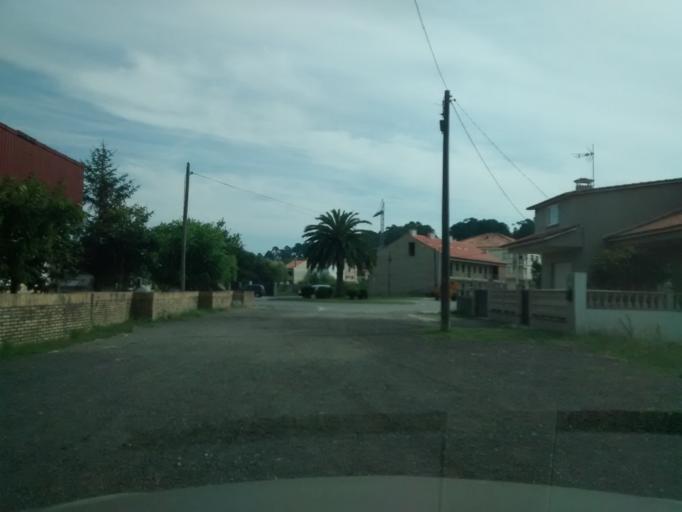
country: ES
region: Galicia
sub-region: Provincia de Pontevedra
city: O Grove
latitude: 42.4812
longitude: -8.8609
